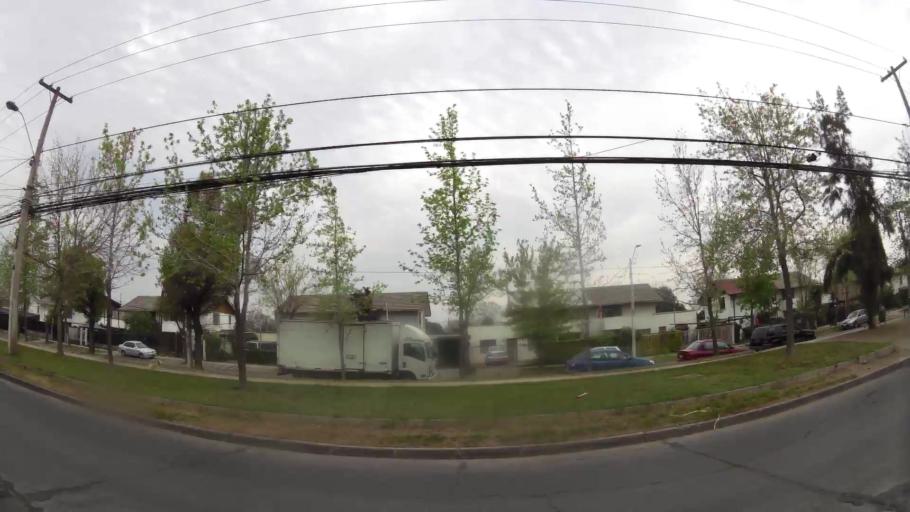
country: CL
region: Santiago Metropolitan
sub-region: Provincia de Santiago
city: Villa Presidente Frei, Nunoa, Santiago, Chile
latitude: -33.4744
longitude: -70.6121
